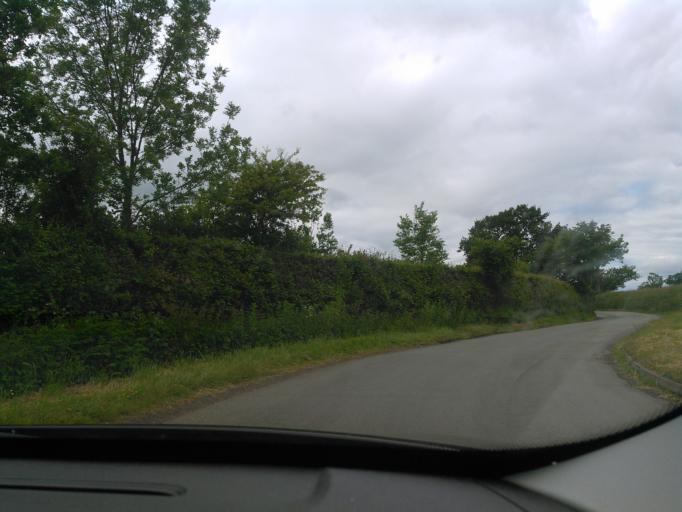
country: GB
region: England
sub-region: Shropshire
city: Wem
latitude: 52.9108
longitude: -2.7312
